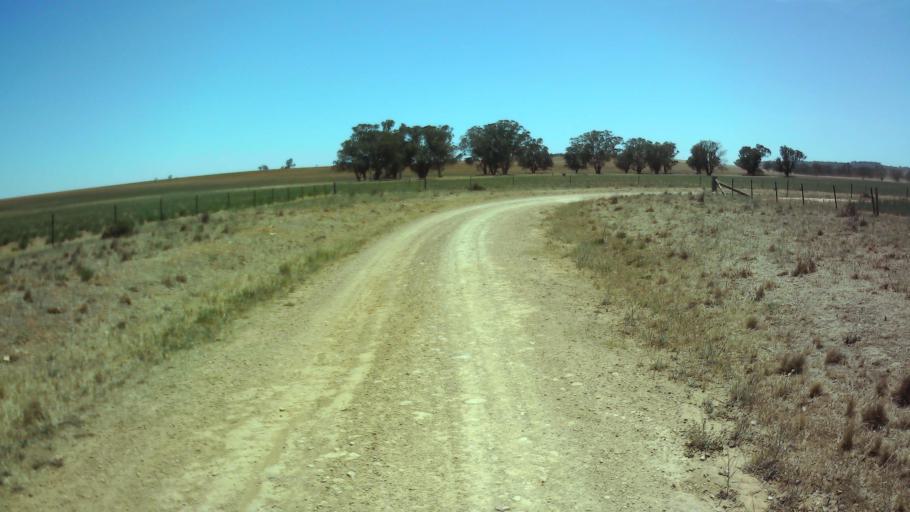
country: AU
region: New South Wales
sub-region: Weddin
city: Grenfell
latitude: -33.9924
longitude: 148.1571
